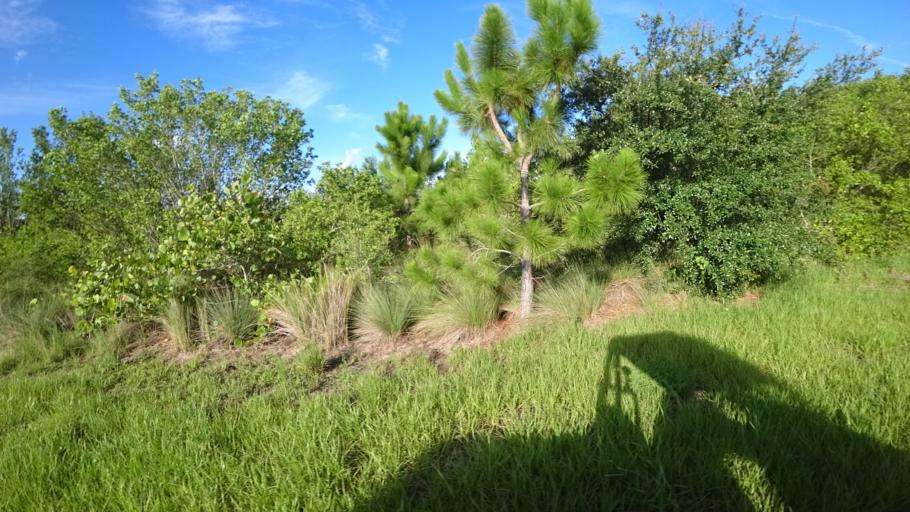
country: US
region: Florida
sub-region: Manatee County
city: Cortez
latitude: 27.5050
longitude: -82.6677
